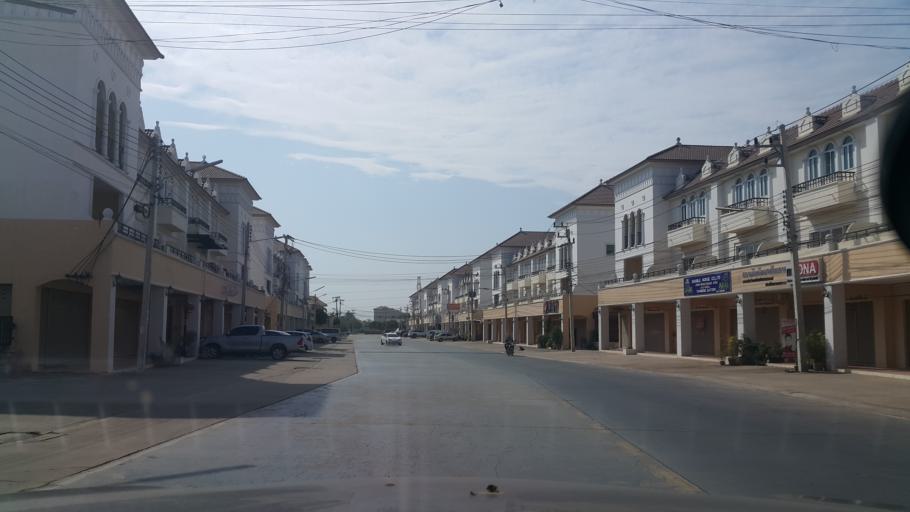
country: TH
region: Nakhon Ratchasima
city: Nakhon Ratchasima
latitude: 14.9864
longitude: 102.0572
